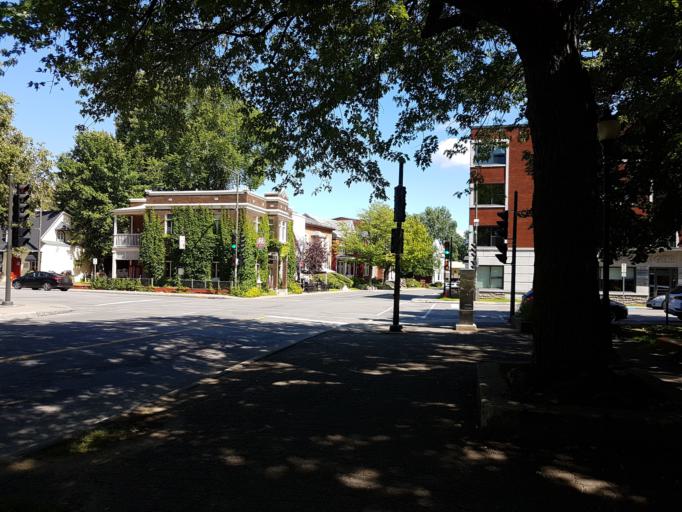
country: CA
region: Quebec
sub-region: Mauricie
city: Trois-Rivieres
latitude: 46.3438
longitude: -72.5421
